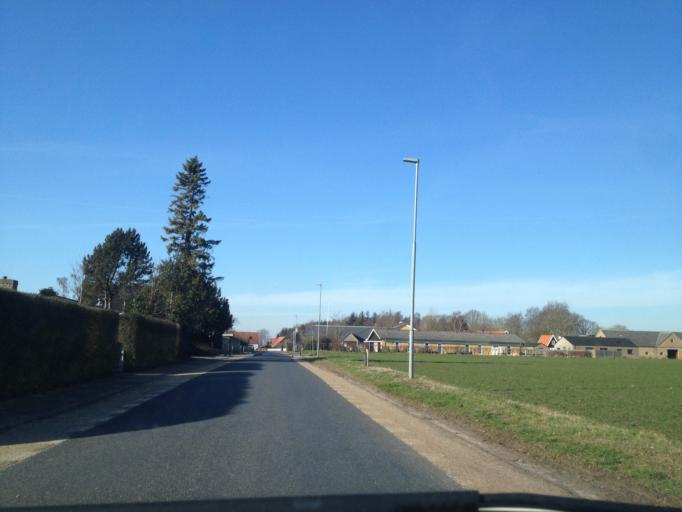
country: DK
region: South Denmark
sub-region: Nyborg Kommune
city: Ullerslev
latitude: 55.3936
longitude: 10.6908
